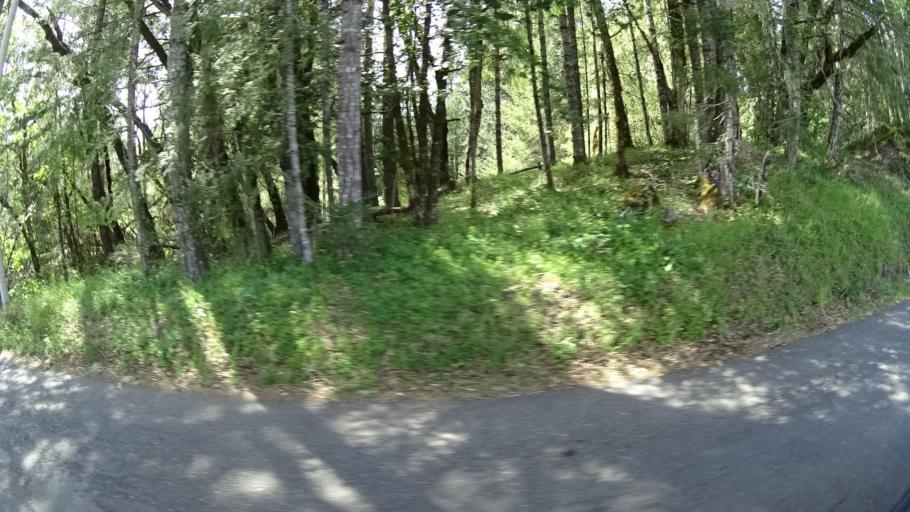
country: US
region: California
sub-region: Humboldt County
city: Redway
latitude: 40.4073
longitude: -123.7512
